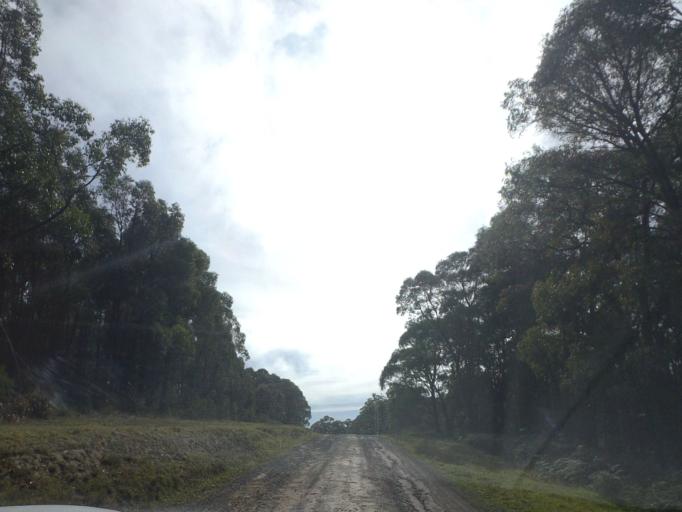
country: AU
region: Victoria
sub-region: Moorabool
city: Bacchus Marsh
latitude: -37.4703
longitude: 144.2143
